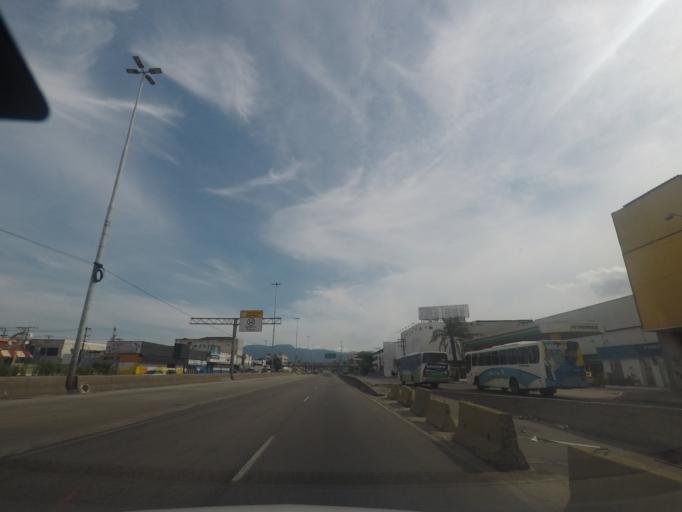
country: BR
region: Rio de Janeiro
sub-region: Rio De Janeiro
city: Rio de Janeiro
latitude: -22.8580
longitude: -43.2479
